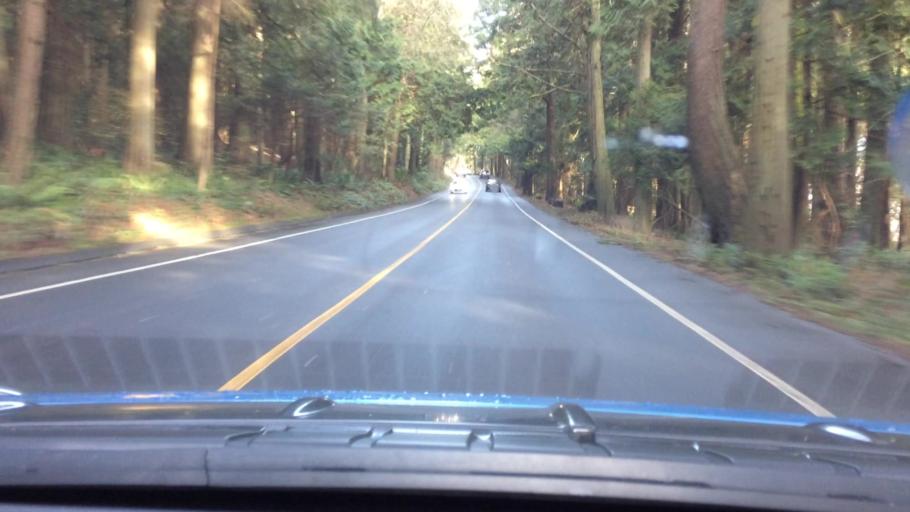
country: CA
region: British Columbia
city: Oak Bay
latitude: 48.4972
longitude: -123.3373
